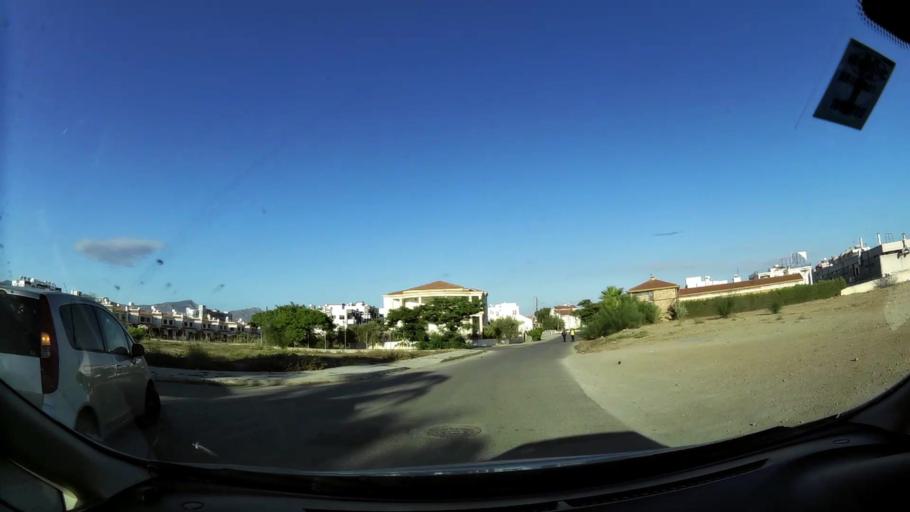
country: CY
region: Lefkosia
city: Nicosia
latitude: 35.1996
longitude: 33.3336
